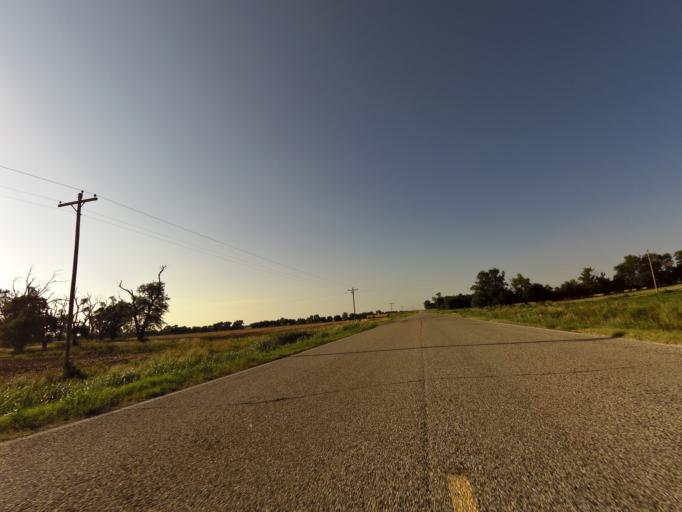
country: US
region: Kansas
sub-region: Reno County
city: Buhler
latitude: 38.1772
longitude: -97.8486
